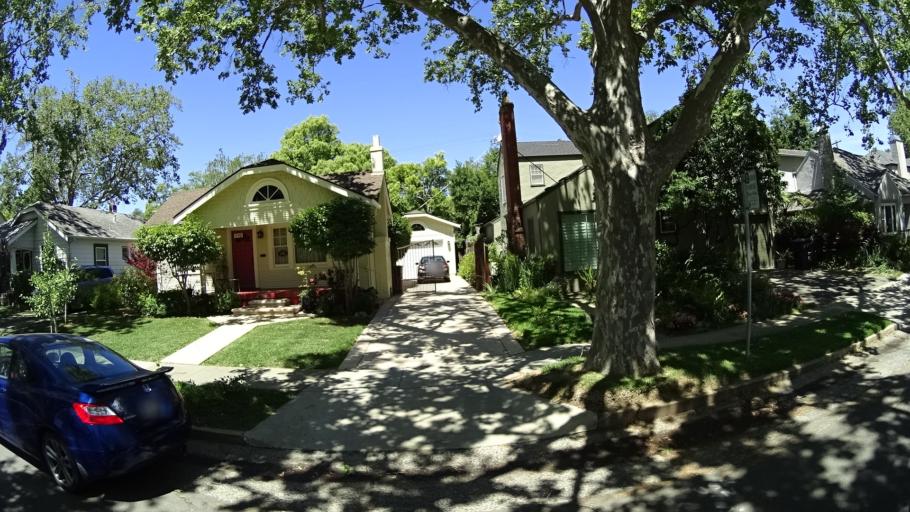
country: US
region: California
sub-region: Sacramento County
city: Sacramento
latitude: 38.5748
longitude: -121.4550
